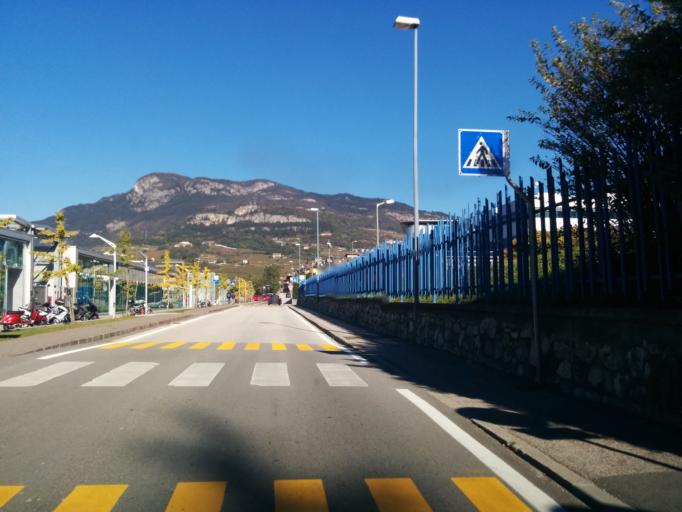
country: IT
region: Trentino-Alto Adige
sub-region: Provincia di Trento
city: Povo
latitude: 46.0666
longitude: 11.1505
